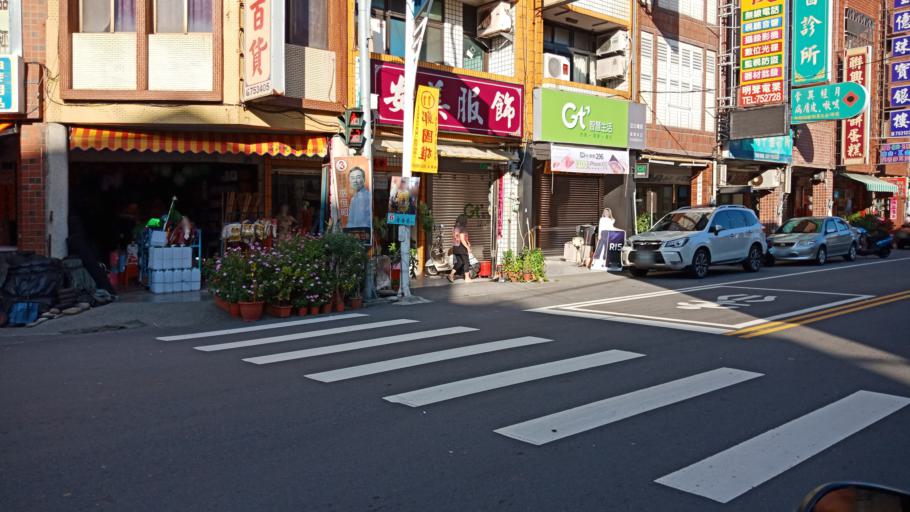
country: TW
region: Taiwan
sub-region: Miaoli
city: Miaoli
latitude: 24.4901
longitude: 120.6810
